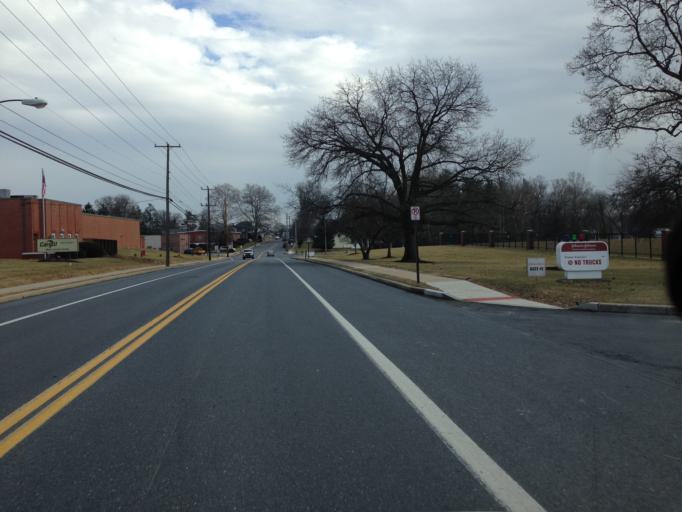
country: US
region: Pennsylvania
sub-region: Lancaster County
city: Lititz
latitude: 40.1617
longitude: -76.3140
